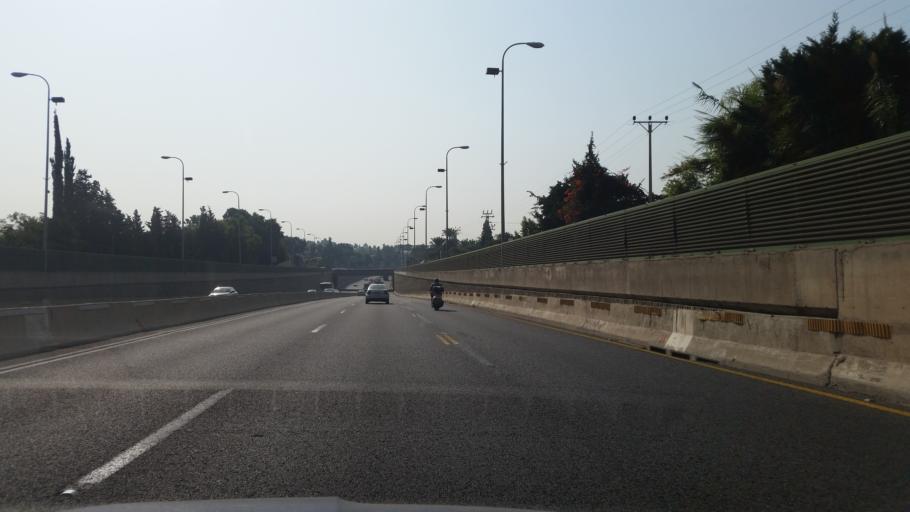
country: IL
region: Tel Aviv
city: Kefar Shemaryahu
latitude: 32.1826
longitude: 34.8154
